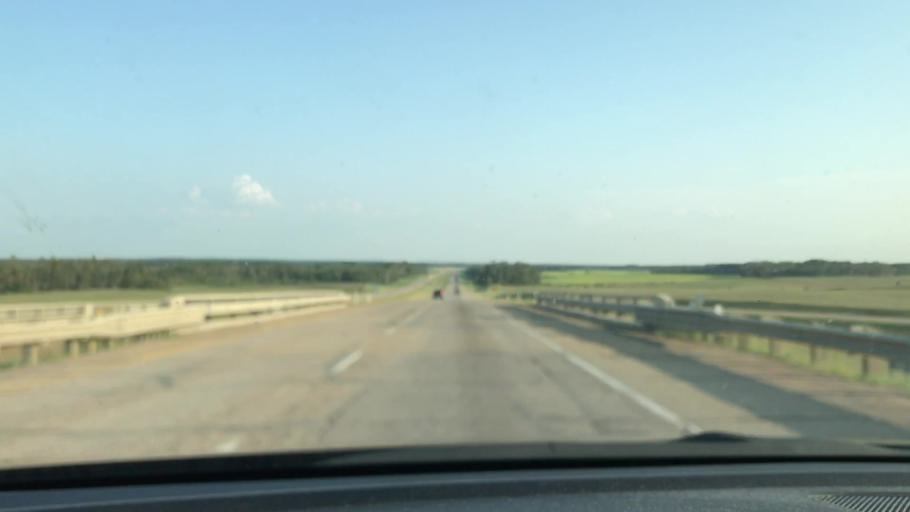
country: CA
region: Alberta
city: Ponoka
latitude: 52.5799
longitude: -113.6632
